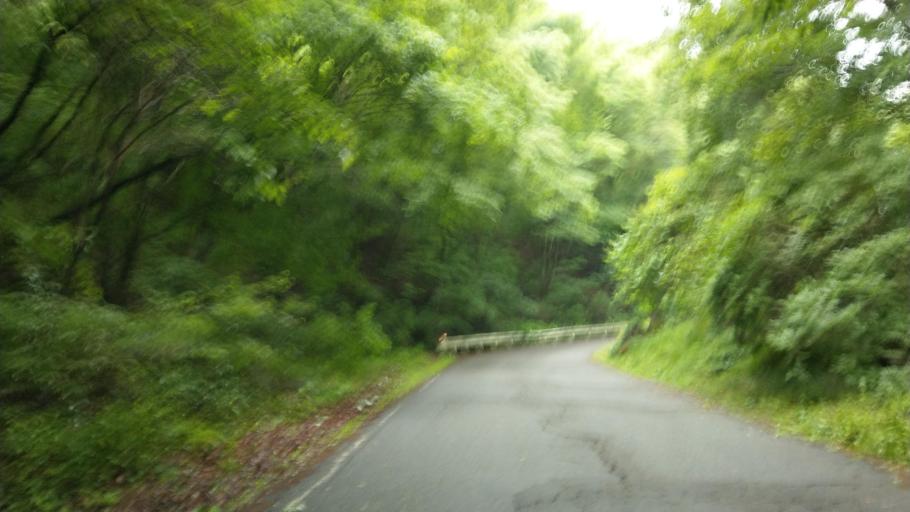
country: JP
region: Nagano
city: Komoro
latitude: 36.3152
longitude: 138.4078
